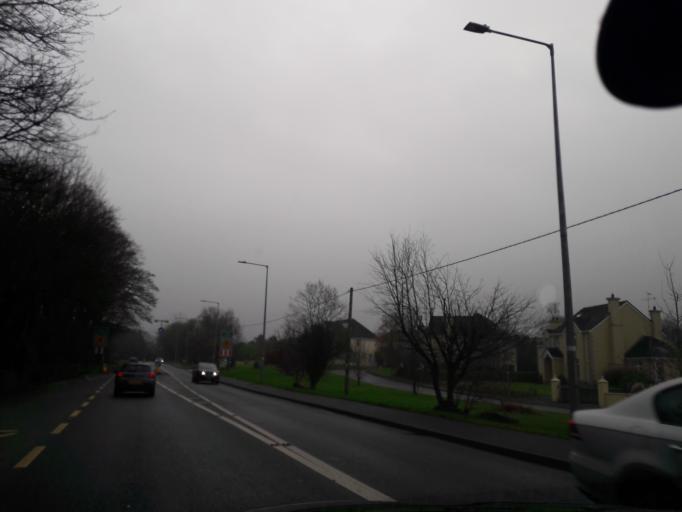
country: IE
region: Ulster
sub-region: County Donegal
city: Leifear
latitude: 54.8402
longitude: -7.4946
